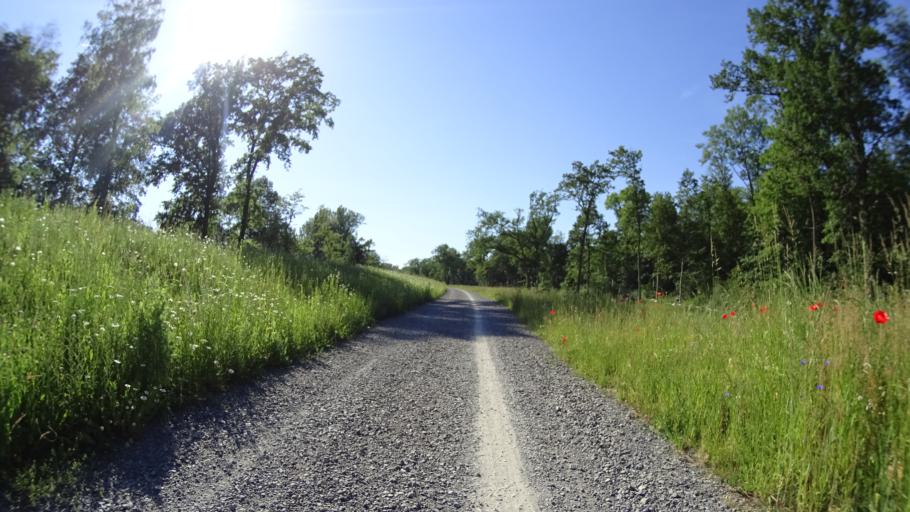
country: DE
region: Baden-Wuerttemberg
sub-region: Karlsruhe Region
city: Eggenstein-Leopoldshafen
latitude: 49.1034
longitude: 8.3796
